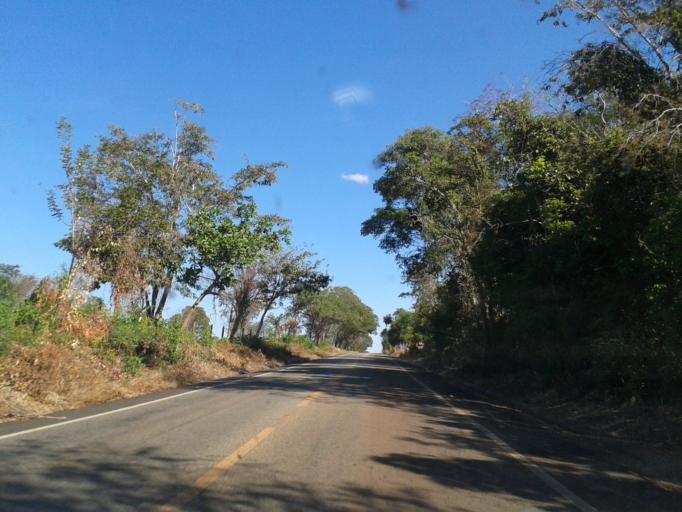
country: BR
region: Goias
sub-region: Mozarlandia
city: Mozarlandia
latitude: -14.6337
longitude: -50.5193
